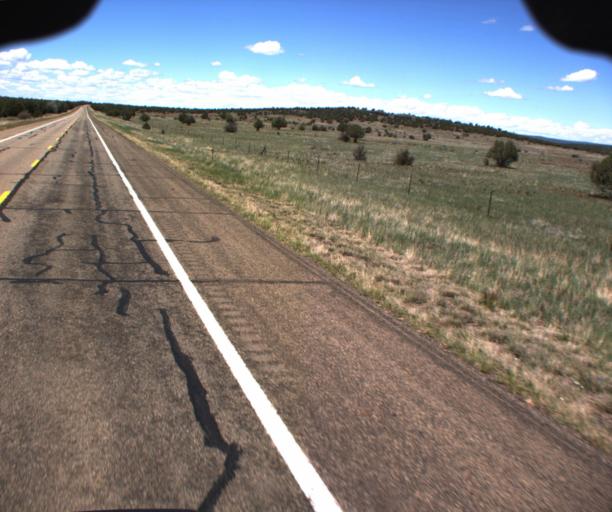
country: US
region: Arizona
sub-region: Yavapai County
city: Paulden
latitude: 35.1523
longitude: -112.4509
